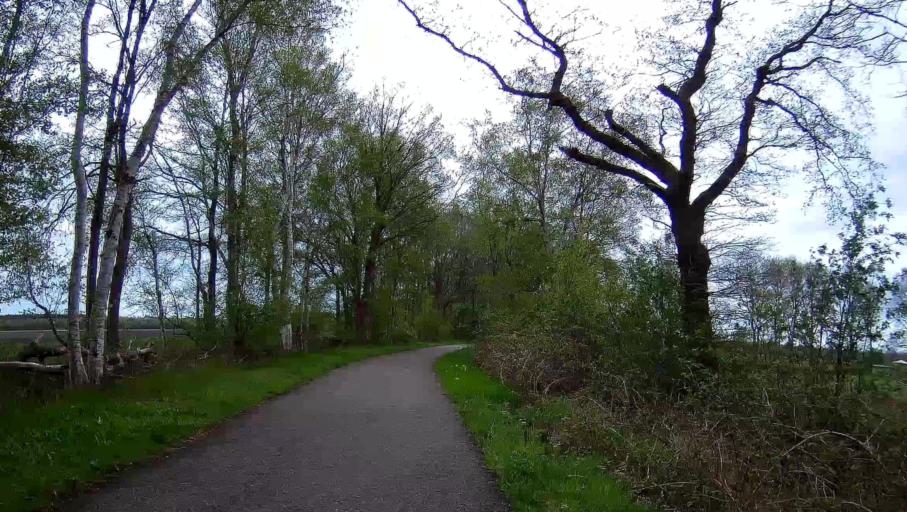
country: NL
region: Drenthe
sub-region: Gemeente Aa en Hunze
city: Anloo
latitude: 52.9654
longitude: 6.7116
